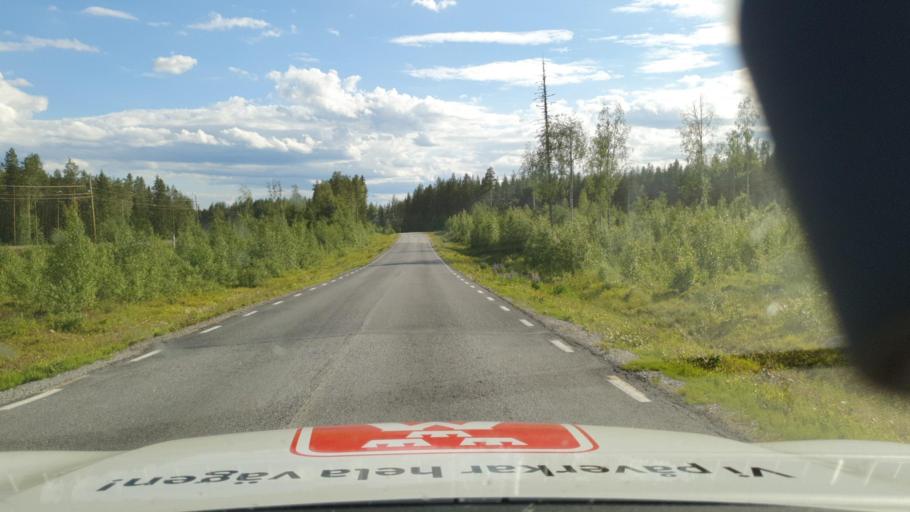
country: SE
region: Vaesterbotten
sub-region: Vindelns Kommun
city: Vindeln
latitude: 64.5569
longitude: 19.9223
